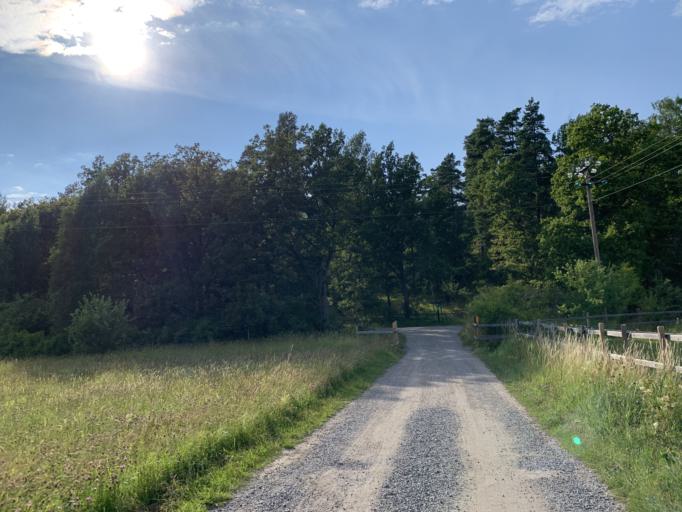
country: SE
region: Stockholm
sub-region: Jarfalla Kommun
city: Jakobsberg
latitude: 59.4426
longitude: 17.8577
